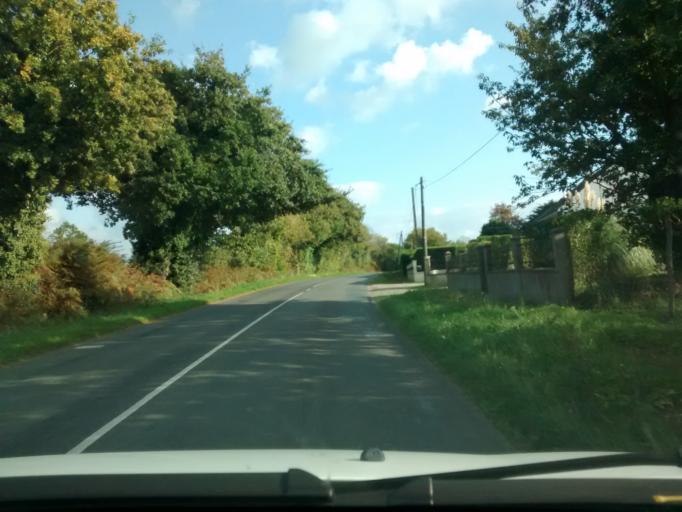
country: FR
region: Pays de la Loire
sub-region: Departement de la Loire-Atlantique
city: Orvault
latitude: 47.2815
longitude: -1.6440
